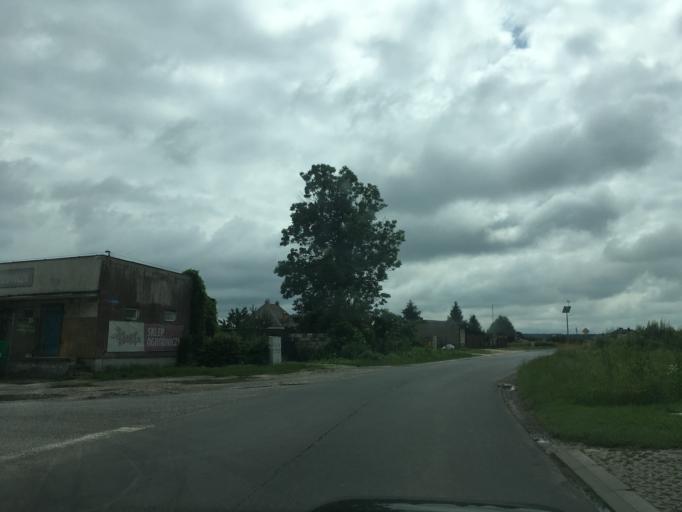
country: PL
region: Lublin Voivodeship
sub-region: Powiat swidnicki
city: Swidnik
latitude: 51.1994
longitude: 22.7296
